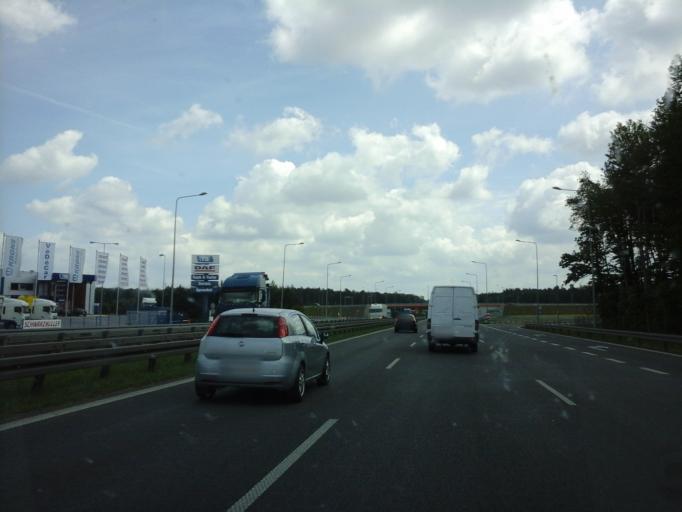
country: PL
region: Lodz Voivodeship
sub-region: Powiat lodzki wschodni
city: Rzgow
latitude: 51.6414
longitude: 19.4959
